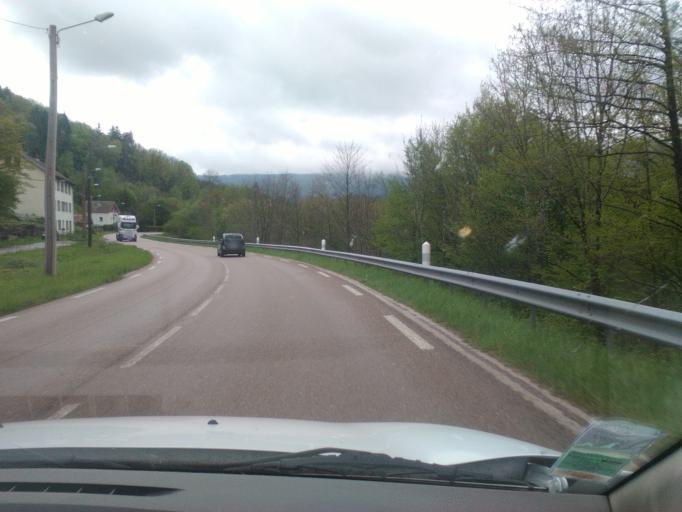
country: FR
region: Lorraine
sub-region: Departement des Vosges
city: Saulxures-sur-Moselotte
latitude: 47.9615
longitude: 6.7371
